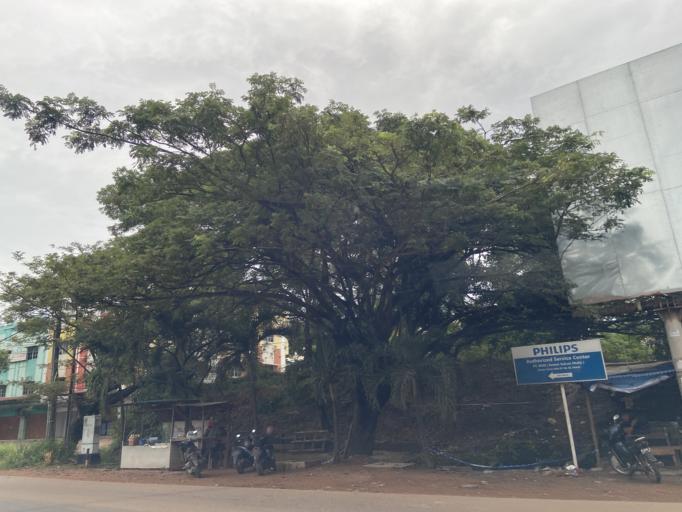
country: SG
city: Singapore
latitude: 1.1627
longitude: 104.0153
